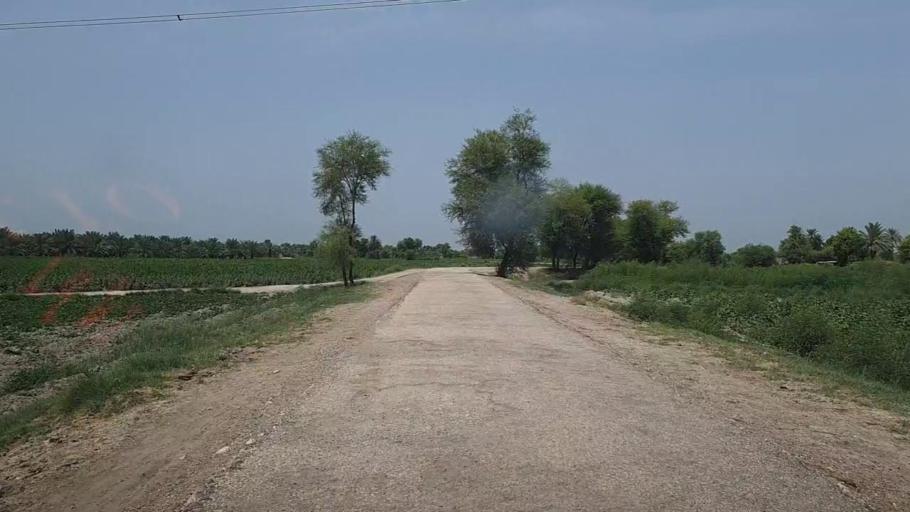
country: PK
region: Sindh
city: Pano Aqil
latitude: 27.8258
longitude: 69.2143
